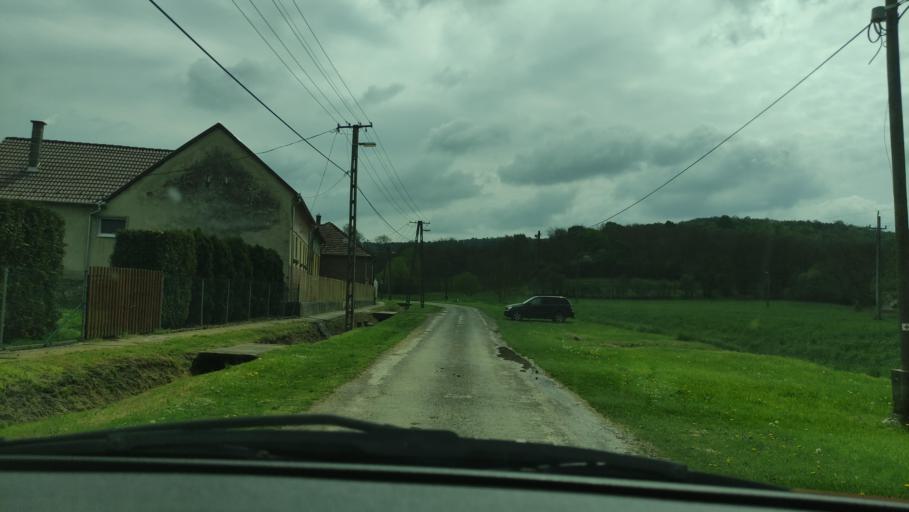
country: HU
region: Baranya
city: Sasd
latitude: 46.2813
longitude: 18.1428
